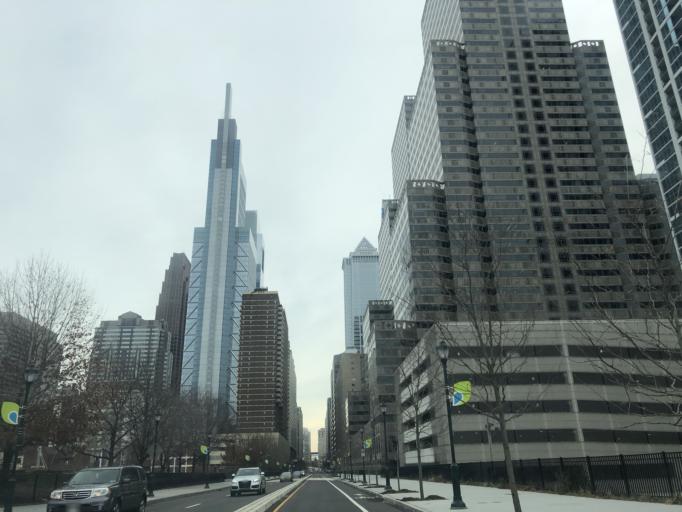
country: US
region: Pennsylvania
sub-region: Philadelphia County
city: Philadelphia
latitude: 39.9550
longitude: -75.1762
